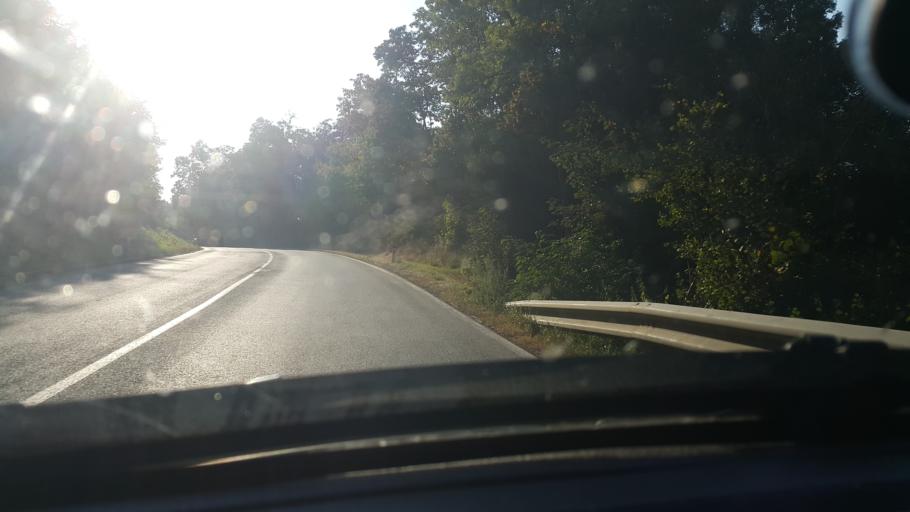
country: AT
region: Carinthia
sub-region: Politischer Bezirk Feldkirchen
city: Glanegg
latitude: 46.6704
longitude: 14.2530
